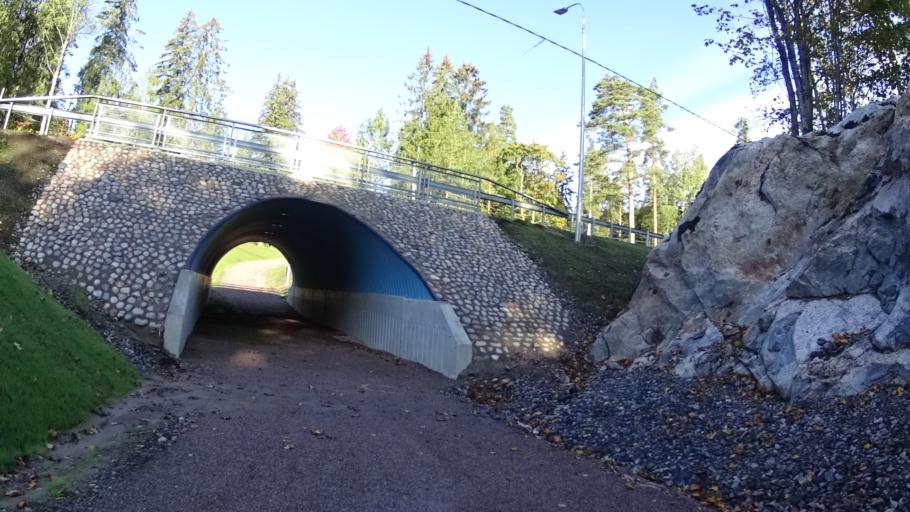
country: FI
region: Uusimaa
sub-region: Helsinki
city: Espoo
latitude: 60.2686
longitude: 24.6537
